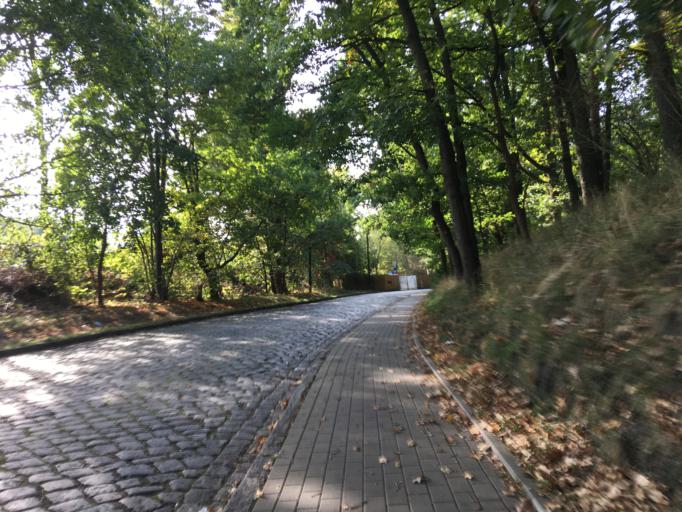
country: DE
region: Brandenburg
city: Hoppegarten
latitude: 52.5174
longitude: 13.6640
